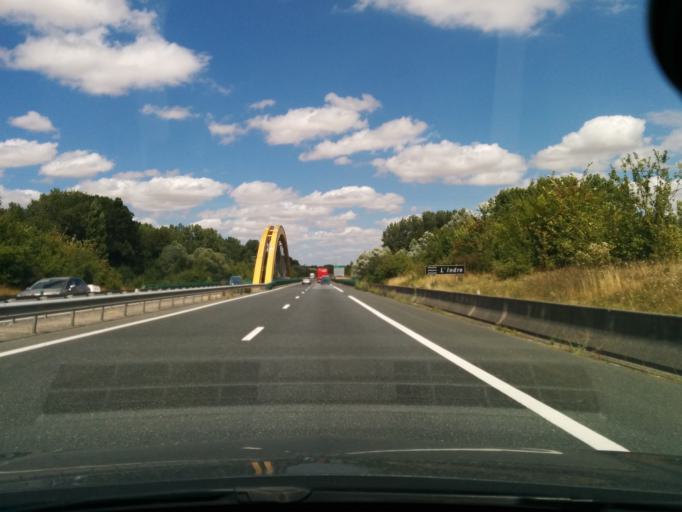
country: FR
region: Centre
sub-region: Departement de l'Indre
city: Saint-Maur
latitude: 46.8134
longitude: 1.6204
